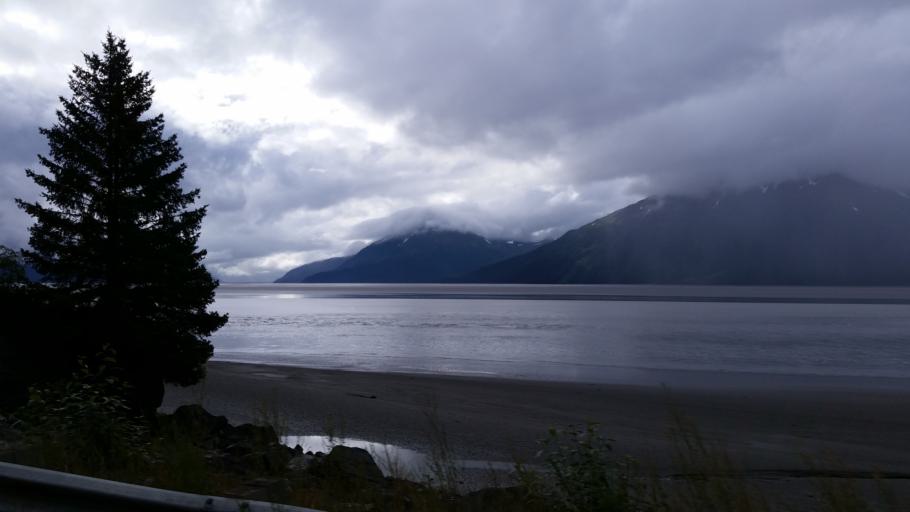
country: US
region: Alaska
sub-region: Anchorage Municipality
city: Girdwood
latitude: 60.9386
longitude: -149.2467
